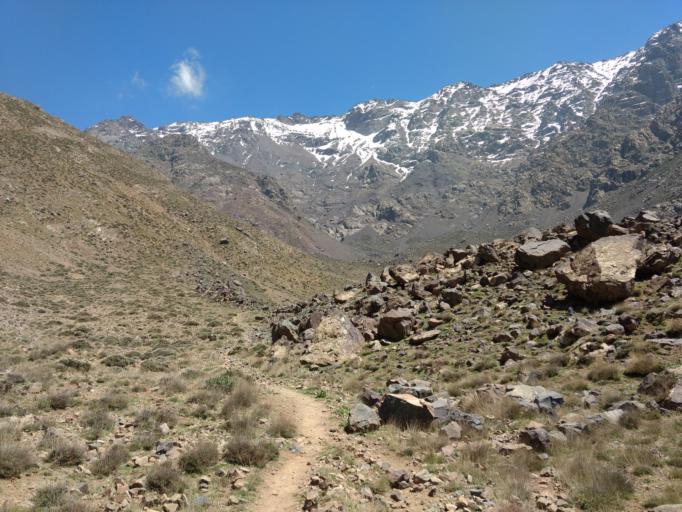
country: MA
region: Marrakech-Tensift-Al Haouz
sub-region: Al-Haouz
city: Moulay Brahim
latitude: 31.1290
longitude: -7.9079
